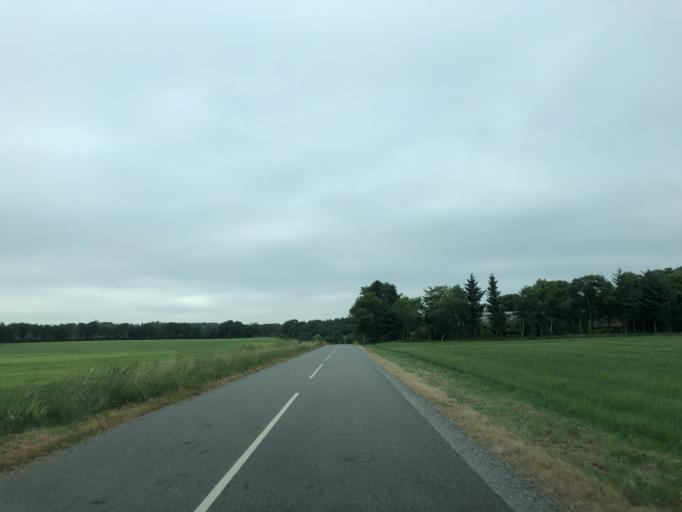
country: DK
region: Central Jutland
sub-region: Holstebro Kommune
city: Holstebro
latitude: 56.2553
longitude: 8.6302
